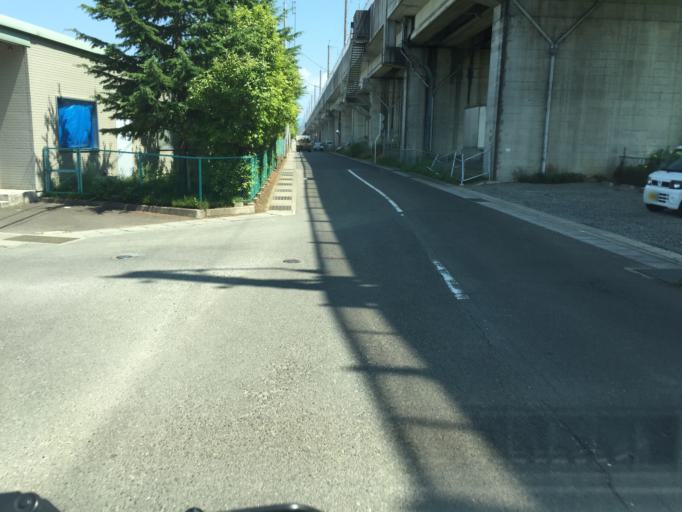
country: JP
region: Fukushima
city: Fukushima-shi
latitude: 37.7217
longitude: 140.4551
